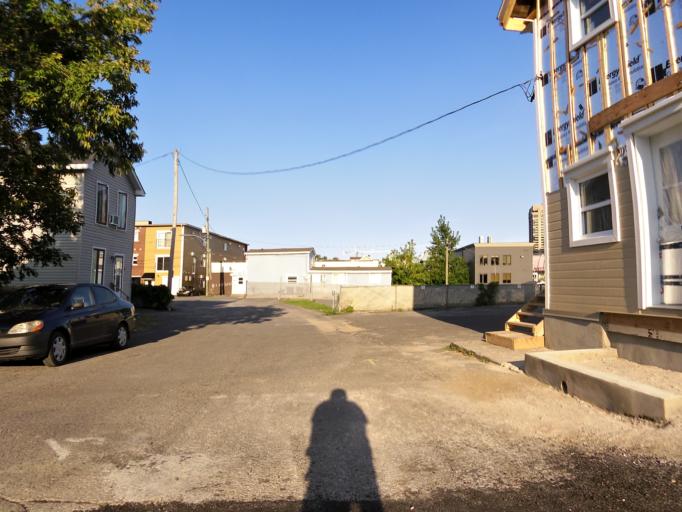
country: CA
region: Ontario
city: Ottawa
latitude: 45.4300
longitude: -75.7215
